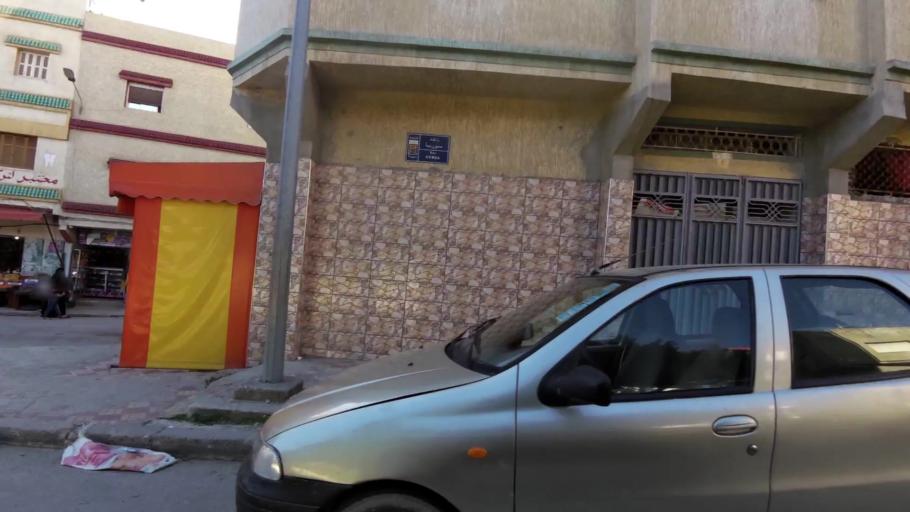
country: MA
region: Tanger-Tetouan
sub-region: Tanger-Assilah
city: Tangier
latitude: 35.7459
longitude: -5.8014
